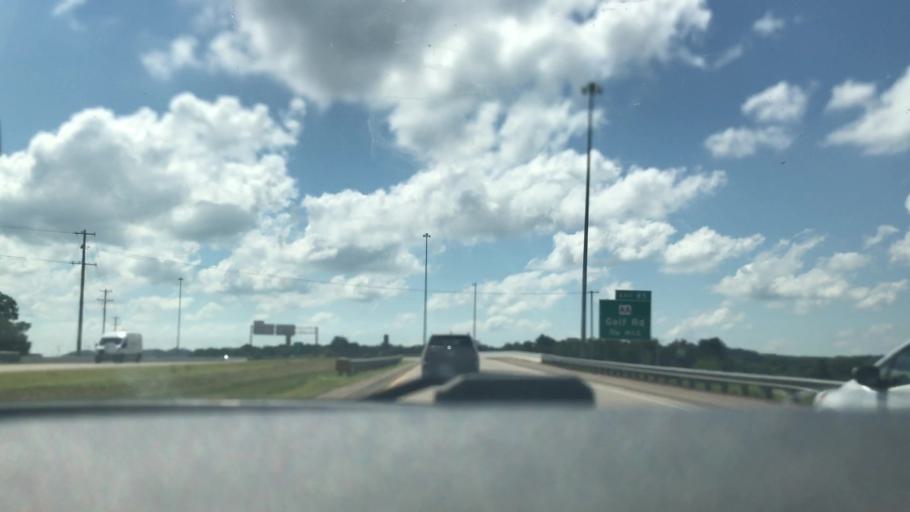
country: US
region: Wisconsin
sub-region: Eau Claire County
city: Altoona
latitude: 44.7886
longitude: -91.4534
